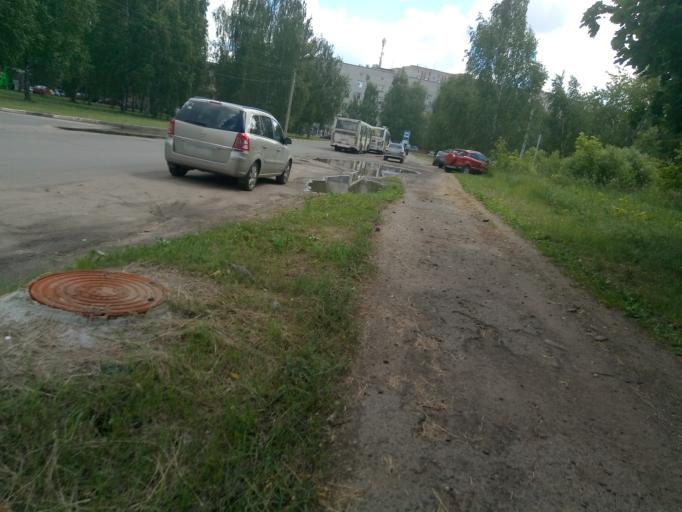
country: RU
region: Jaroslavl
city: Yaroslavl
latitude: 57.6576
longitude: 39.9663
